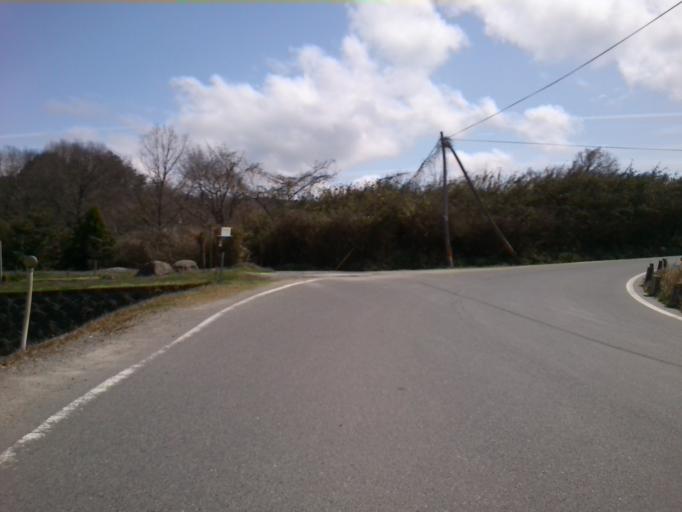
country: JP
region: Nara
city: Nara-shi
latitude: 34.7143
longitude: 135.8886
